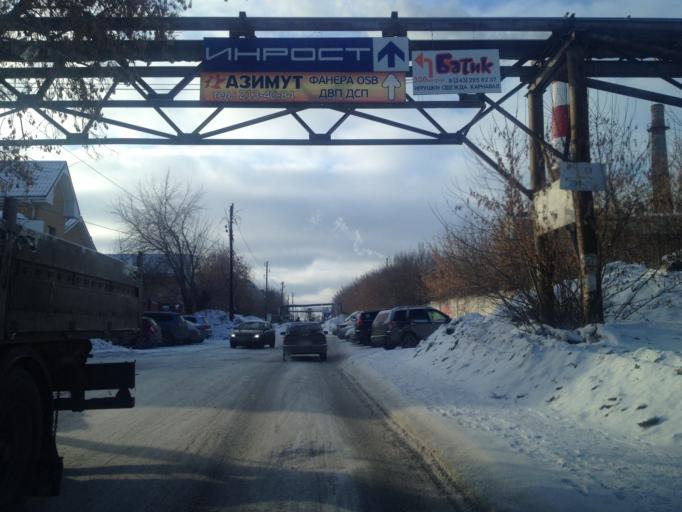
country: RU
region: Sverdlovsk
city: Sovkhoznyy
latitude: 56.7655
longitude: 60.6230
